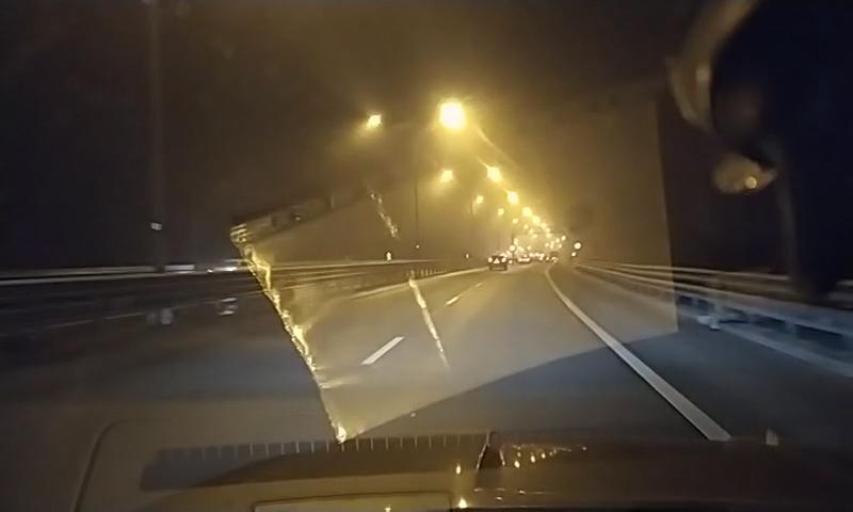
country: RU
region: Leningrad
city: Bugry
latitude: 60.1137
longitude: 30.3866
